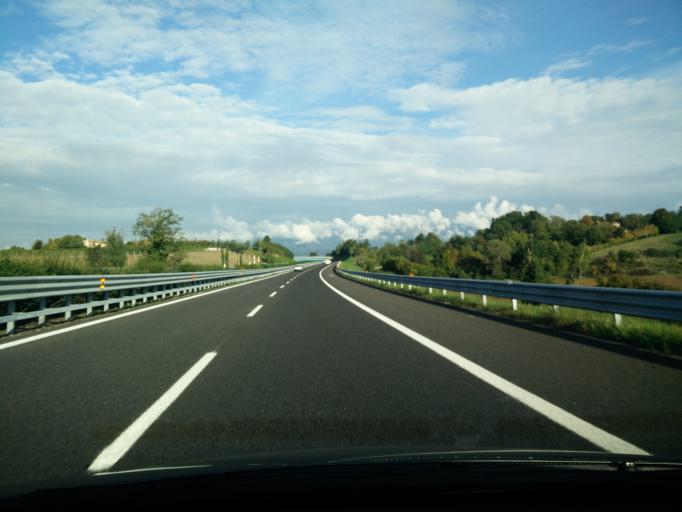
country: IT
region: Veneto
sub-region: Provincia di Treviso
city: San Martino
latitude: 45.9119
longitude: 12.3362
